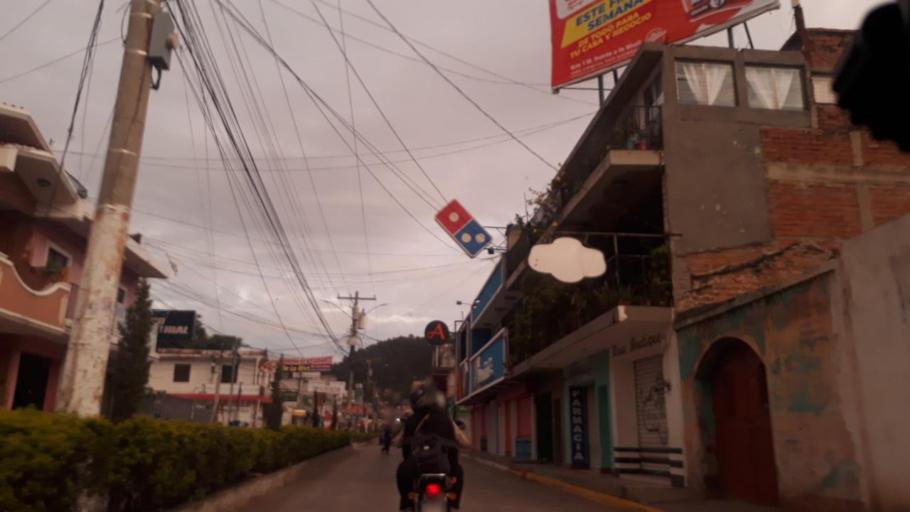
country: GT
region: Jutiapa
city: Jutiapa
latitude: 14.2922
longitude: -89.8993
